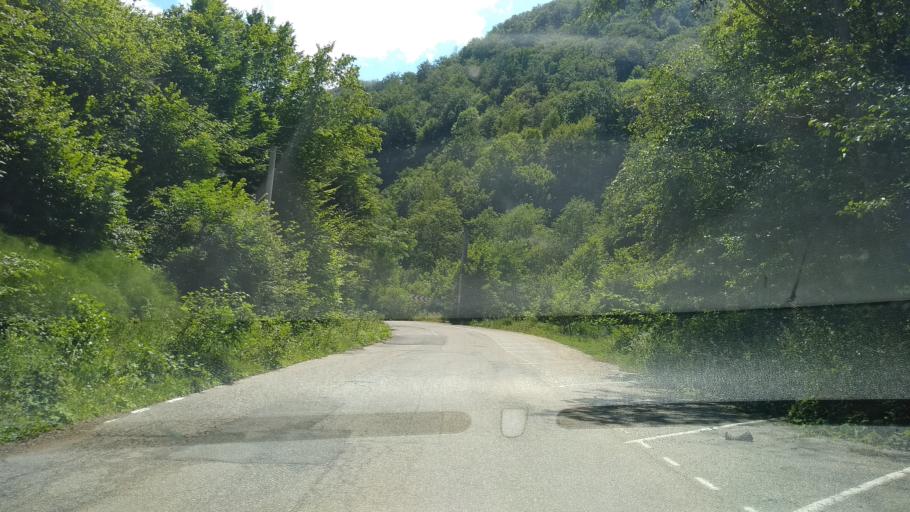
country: RO
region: Hunedoara
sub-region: Comuna Orastioara de Sus
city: Orastioara de Sus
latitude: 45.6600
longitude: 23.1813
